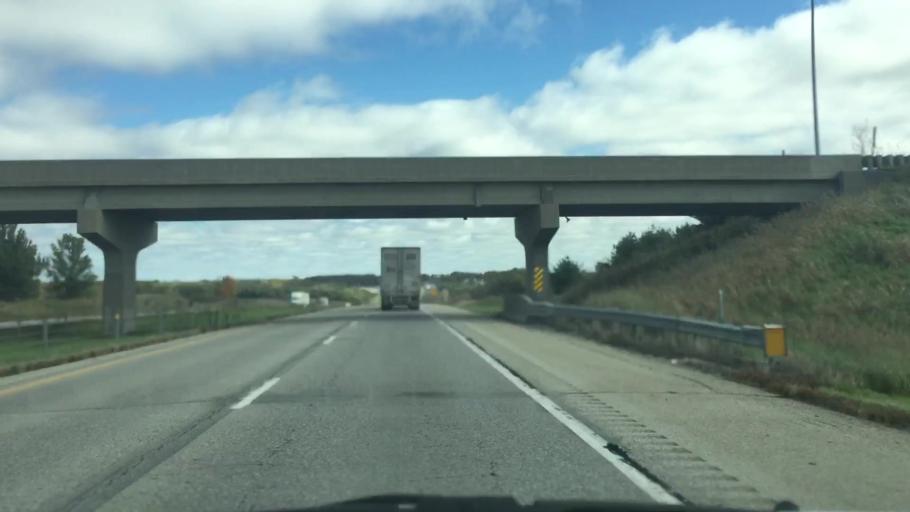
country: US
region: Iowa
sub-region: Poweshiek County
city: Grinnell
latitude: 41.6951
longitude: -92.7943
